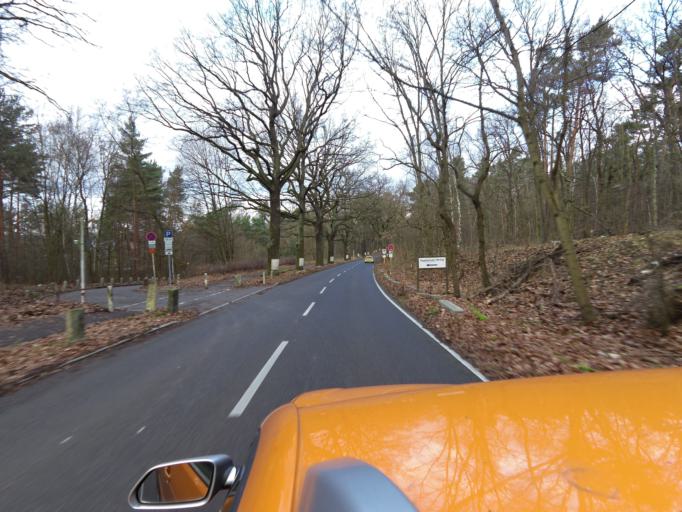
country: DE
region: Berlin
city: Nikolassee
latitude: 52.4510
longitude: 13.1932
